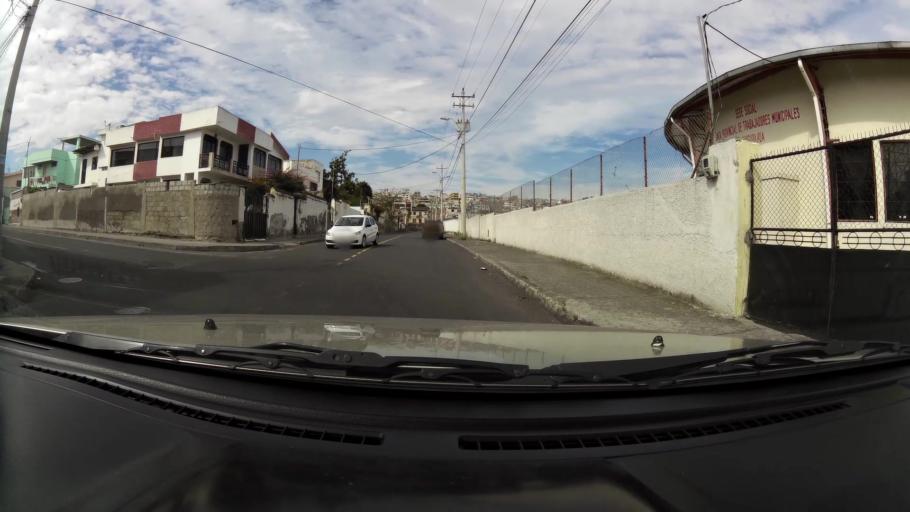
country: EC
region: Tungurahua
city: Ambato
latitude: -1.2431
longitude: -78.6228
